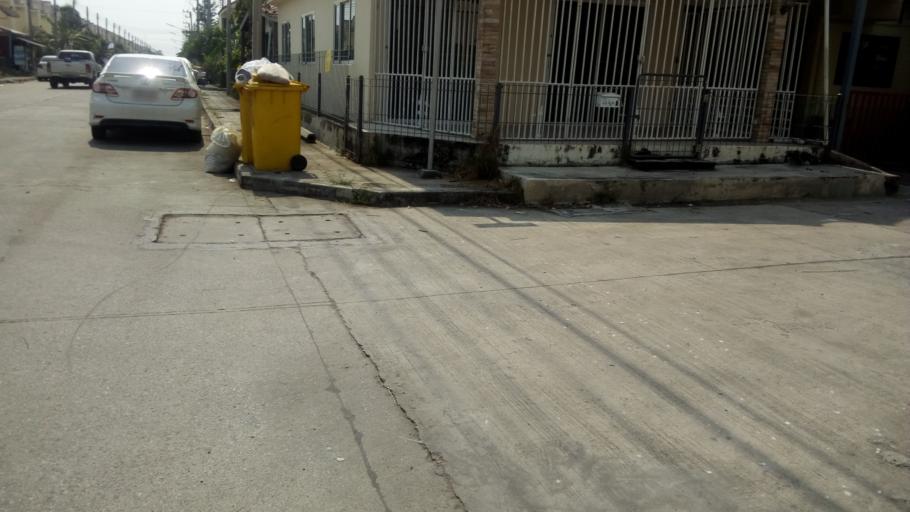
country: TH
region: Pathum Thani
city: Nong Suea
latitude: 14.0546
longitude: 100.8414
